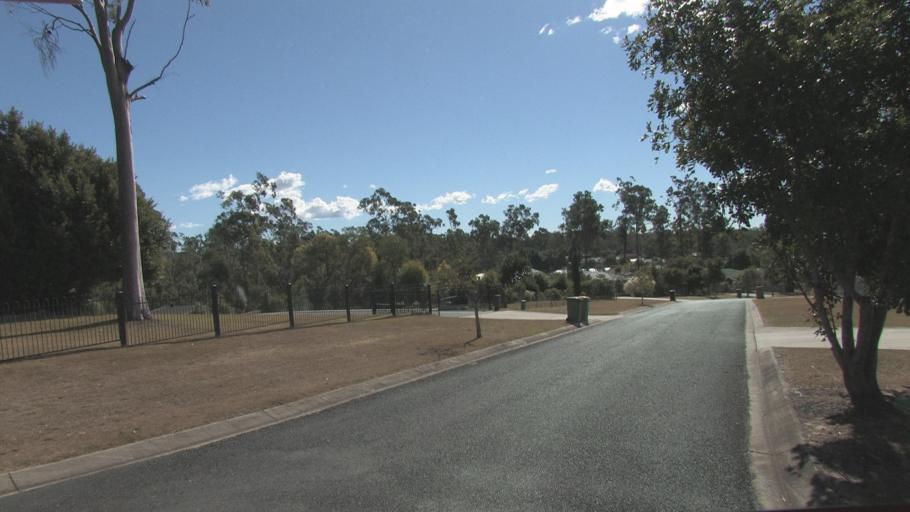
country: AU
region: Queensland
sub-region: Logan
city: North Maclean
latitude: -27.7524
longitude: 152.9376
